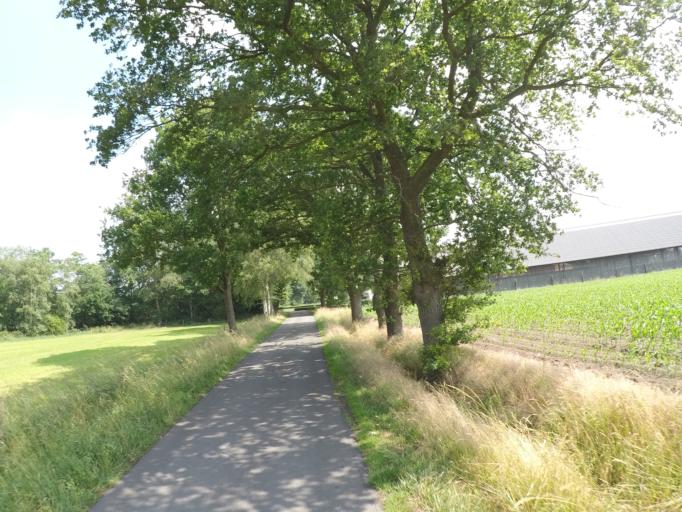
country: BE
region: Flanders
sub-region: Provincie Antwerpen
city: Brecht
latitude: 51.3619
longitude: 4.6162
